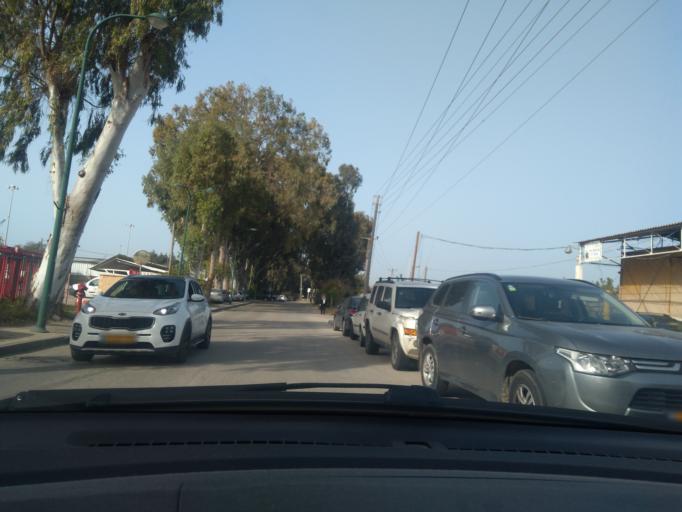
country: IL
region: Central District
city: Netanya
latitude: 32.3215
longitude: 34.8682
